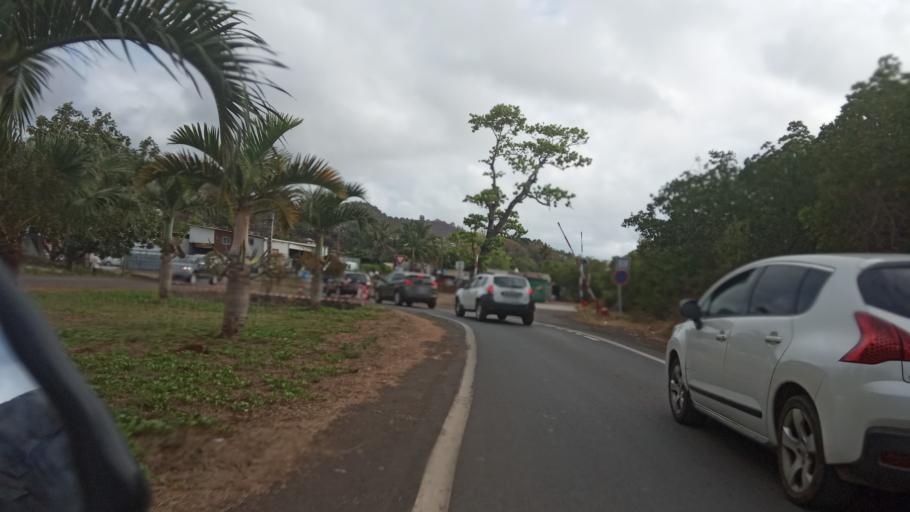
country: YT
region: Mamoudzou
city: Mamoudzou
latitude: -12.7971
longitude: 45.2160
